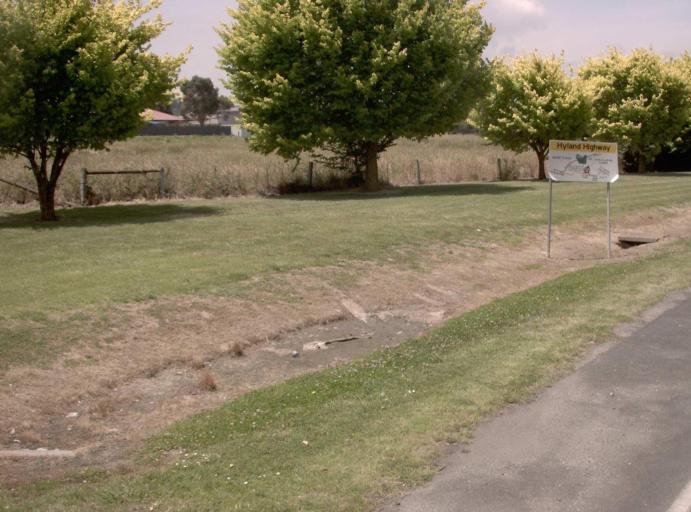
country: AU
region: Victoria
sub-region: Latrobe
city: Traralgon
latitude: -38.2018
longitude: 146.5446
